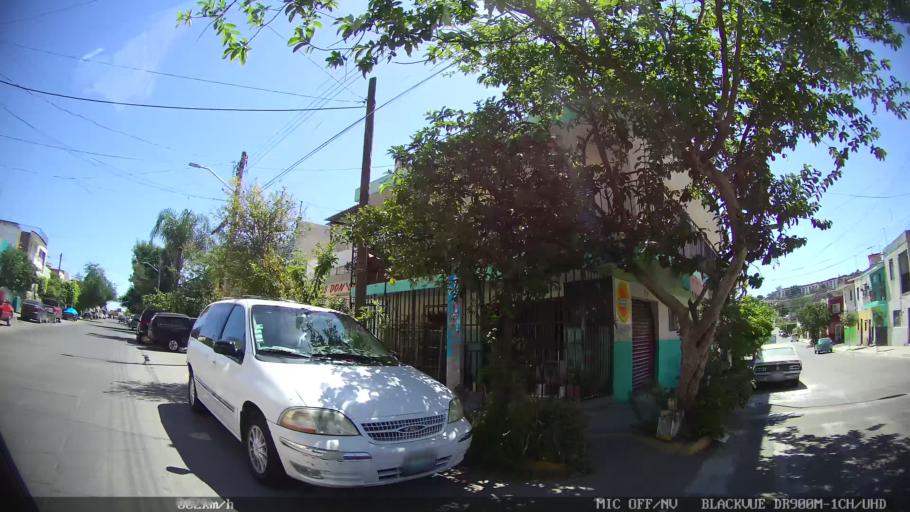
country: MX
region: Jalisco
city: Tlaquepaque
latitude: 20.6886
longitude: -103.2865
